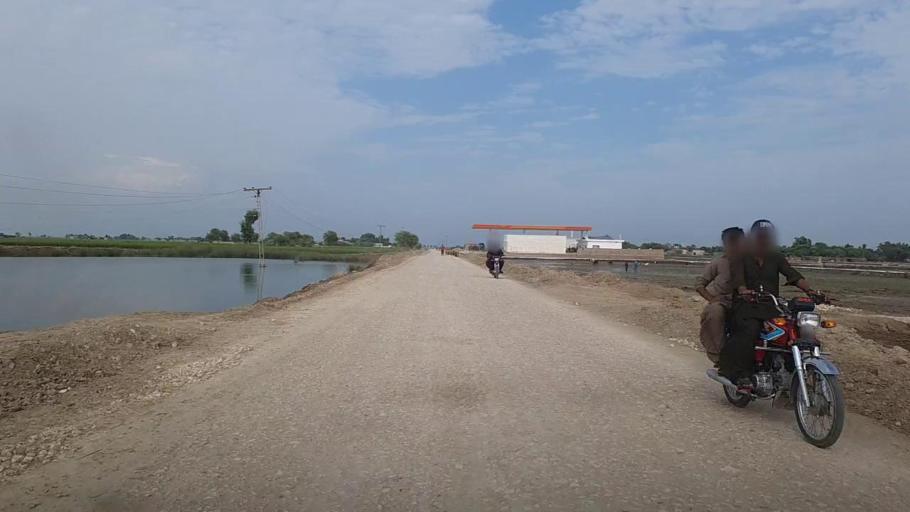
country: PK
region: Sindh
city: Thul
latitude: 28.2566
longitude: 68.8080
